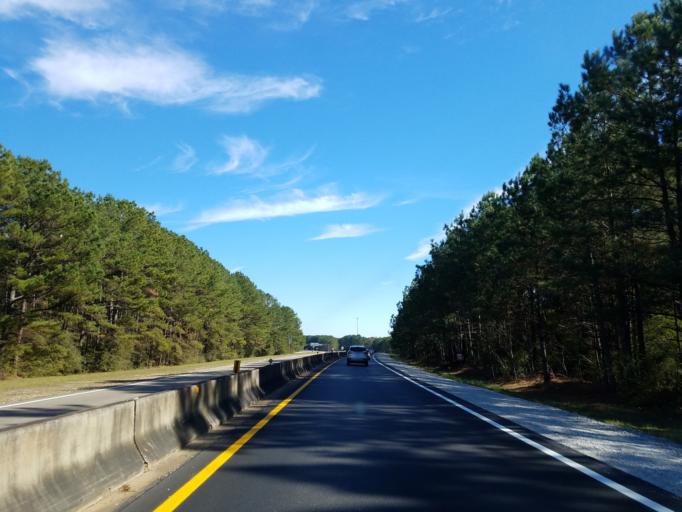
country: US
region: Mississippi
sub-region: Forrest County
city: Hattiesburg
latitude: 31.2397
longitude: -89.3223
